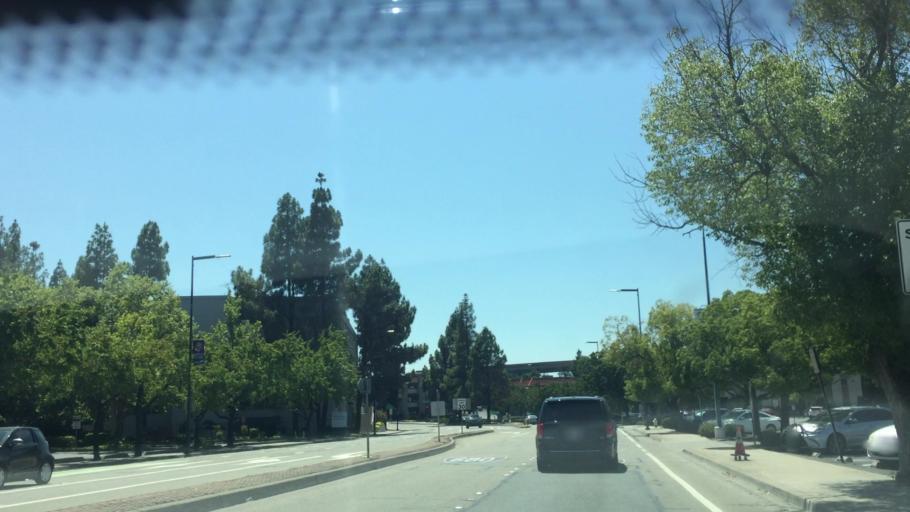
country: US
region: California
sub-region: Contra Costa County
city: Walnut Creek
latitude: 37.8960
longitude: -122.0632
